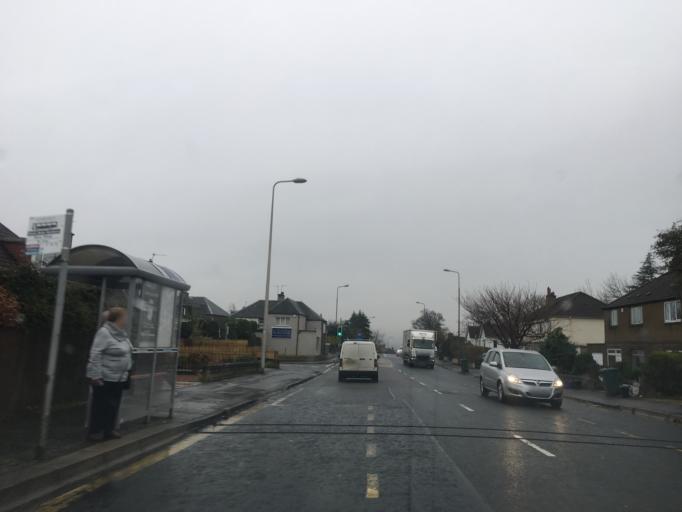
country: GB
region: Scotland
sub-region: Edinburgh
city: Currie
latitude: 55.9489
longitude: -3.2950
